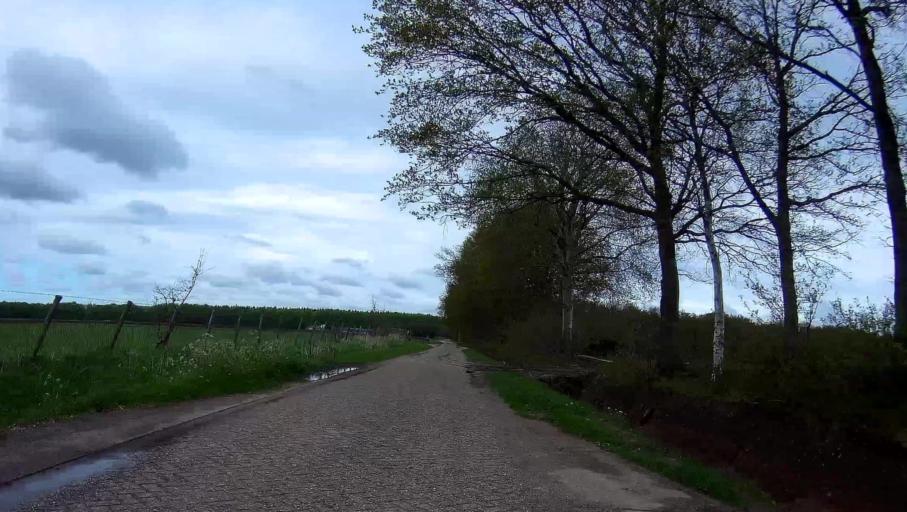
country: NL
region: Drenthe
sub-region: Gemeente Borger-Odoorn
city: Borger
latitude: 52.9437
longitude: 6.7791
